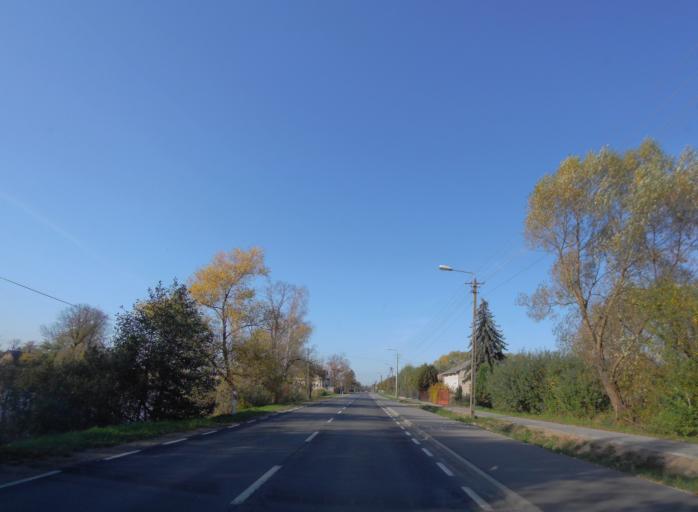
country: PL
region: Masovian Voivodeship
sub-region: Powiat minski
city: Halinow
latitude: 52.1909
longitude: 21.3537
